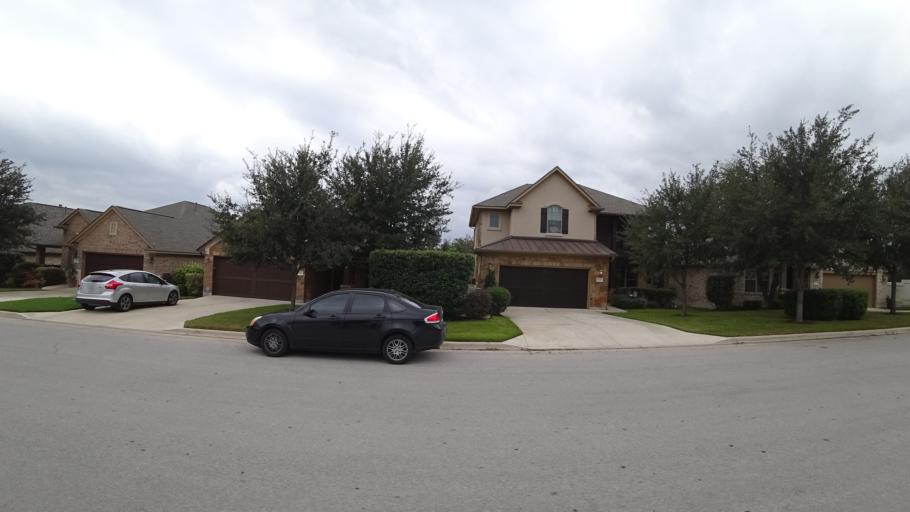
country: US
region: Texas
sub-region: Travis County
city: Bee Cave
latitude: 30.3459
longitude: -97.9174
